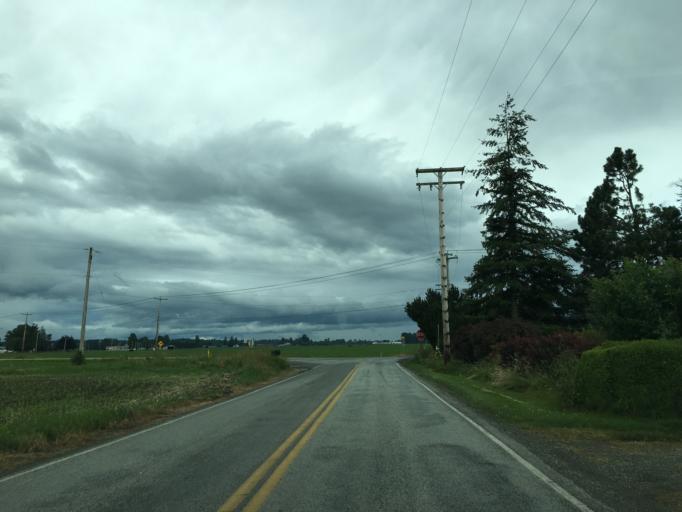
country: US
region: Washington
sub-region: Whatcom County
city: Sumas
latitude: 48.9751
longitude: -122.2584
